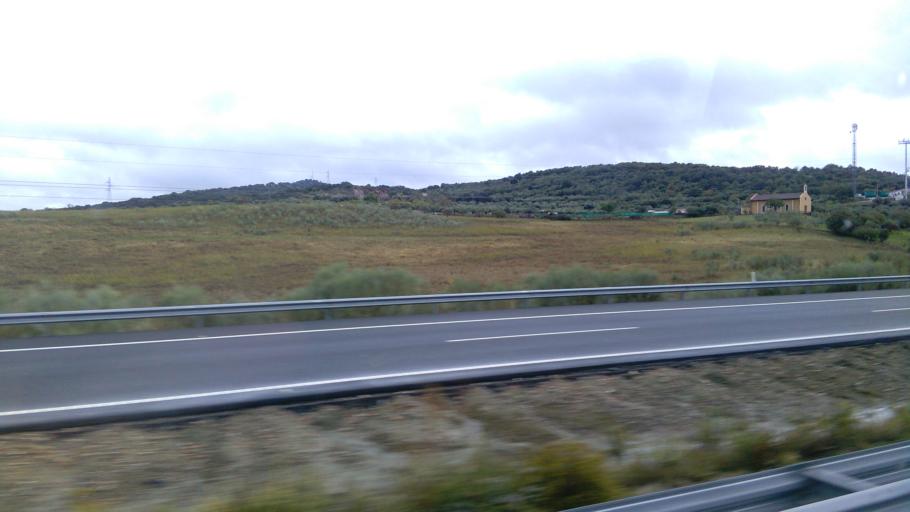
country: ES
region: Extremadura
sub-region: Provincia de Caceres
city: Almaraz
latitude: 39.8147
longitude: -5.6654
